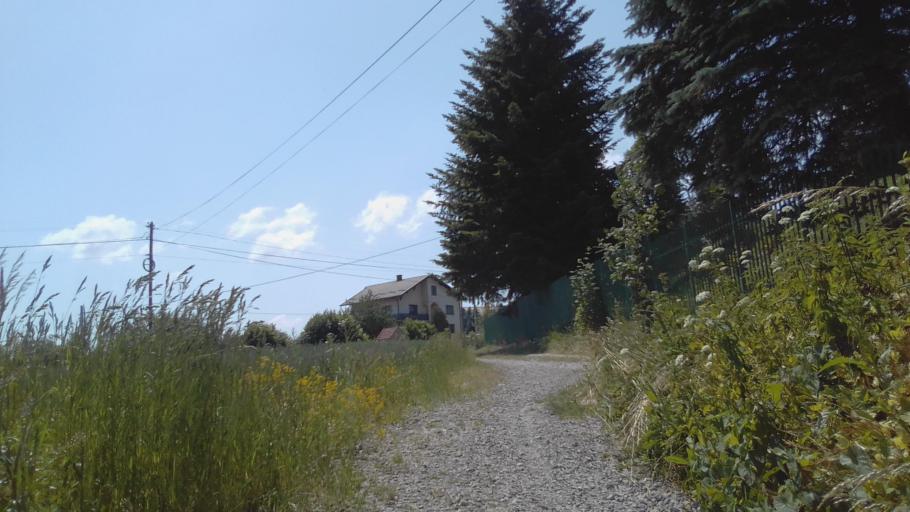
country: PL
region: Subcarpathian Voivodeship
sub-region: Powiat strzyzowski
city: Strzyzow
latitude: 49.8572
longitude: 21.7819
